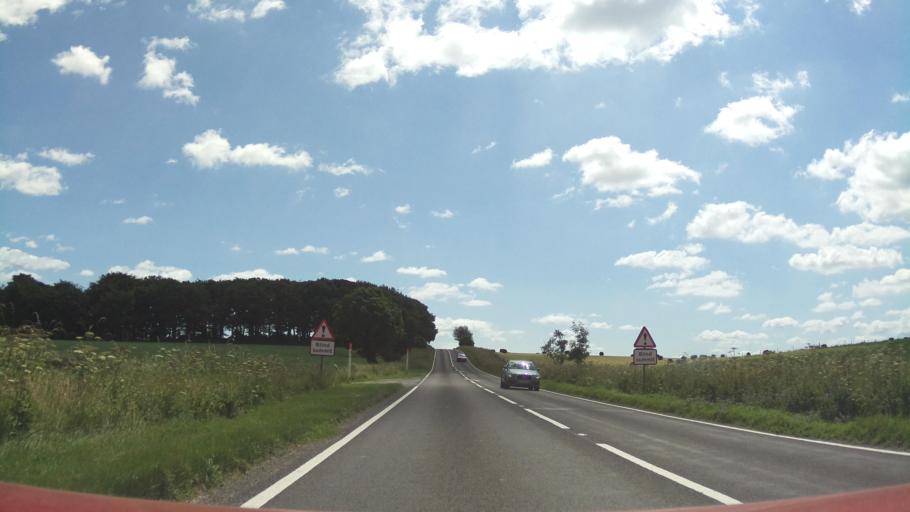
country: GB
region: England
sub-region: Derbyshire
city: Bakewell
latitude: 53.1580
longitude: -1.7723
